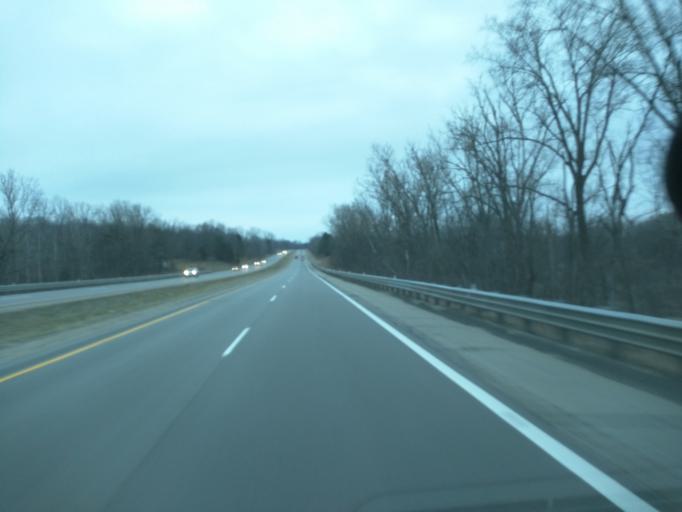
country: US
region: Michigan
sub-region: Ingham County
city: Leslie
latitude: 42.4277
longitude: -84.4379
